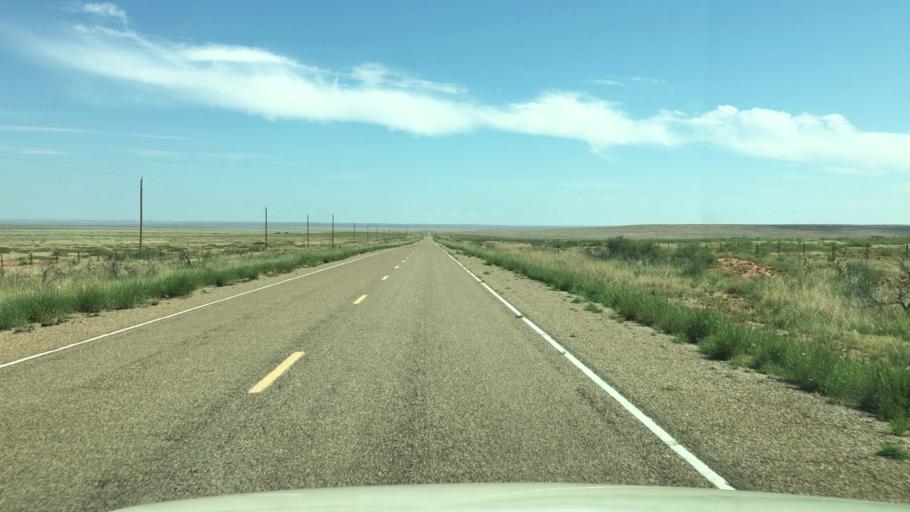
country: US
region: New Mexico
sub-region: De Baca County
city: Fort Sumner
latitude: 33.9894
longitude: -104.5710
